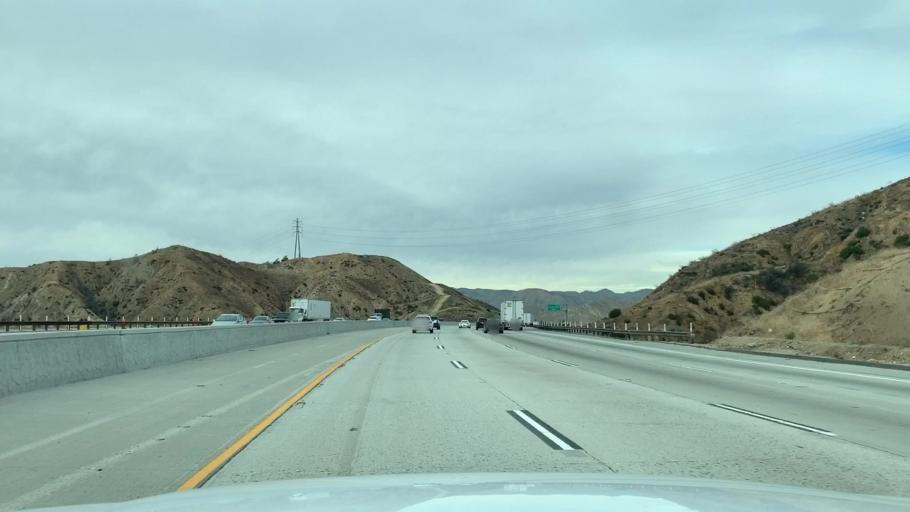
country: US
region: California
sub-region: Los Angeles County
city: Burbank
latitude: 34.2459
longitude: -118.3209
